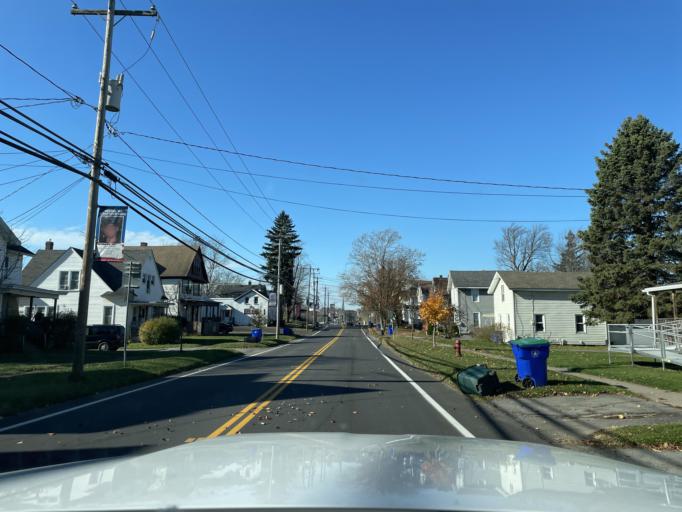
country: US
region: New York
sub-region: Orleans County
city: Medina
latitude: 43.2206
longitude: -78.3780
